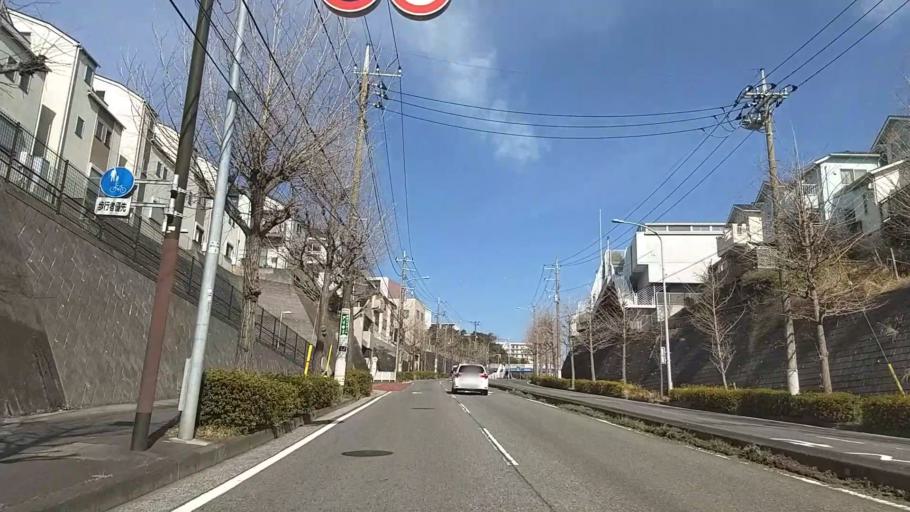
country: JP
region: Kanagawa
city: Kamakura
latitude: 35.3851
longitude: 139.5756
